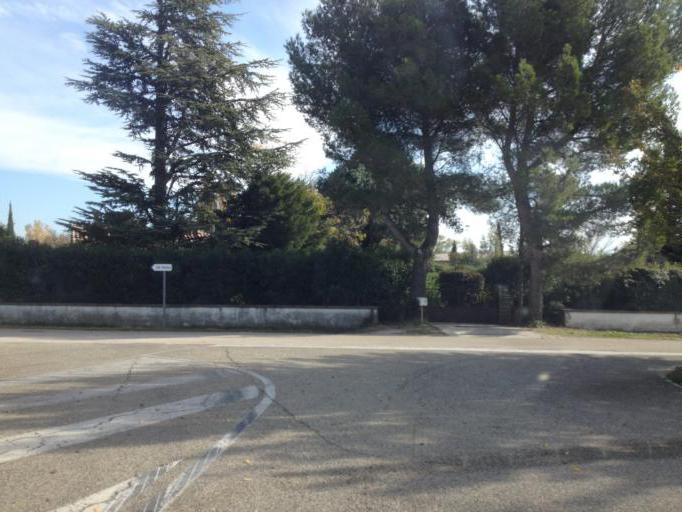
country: FR
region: Provence-Alpes-Cote d'Azur
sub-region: Departement du Vaucluse
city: Courthezon
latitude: 44.0973
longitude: 4.8825
